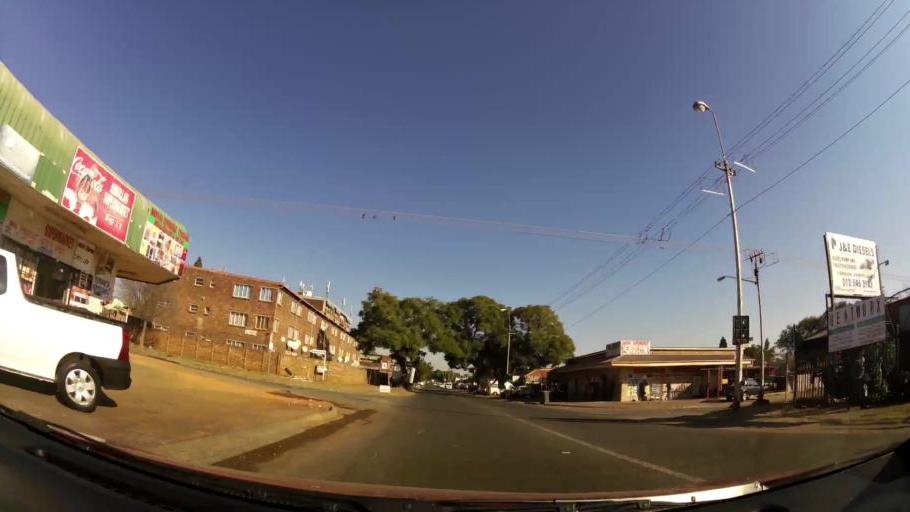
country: ZA
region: Gauteng
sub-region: City of Tshwane Metropolitan Municipality
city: Pretoria
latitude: -25.6653
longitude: 28.1626
